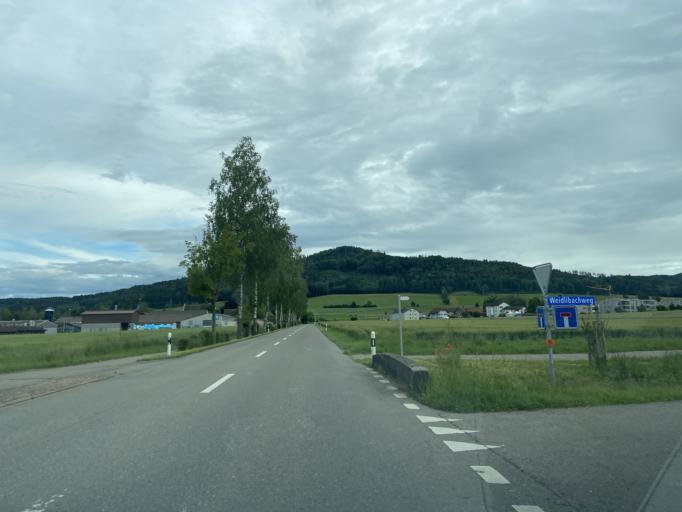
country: CH
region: Thurgau
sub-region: Muenchwilen District
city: Aadorf
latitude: 47.4832
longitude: 8.9047
